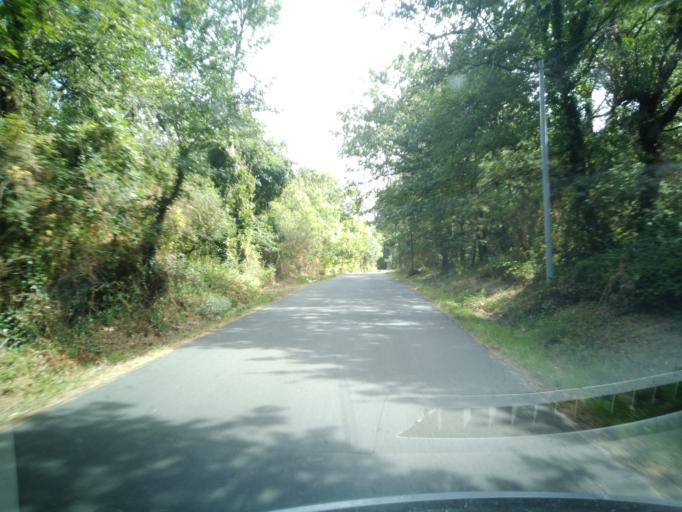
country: FR
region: Poitou-Charentes
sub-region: Departement de la Charente-Maritime
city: Chaillevette
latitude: 45.7164
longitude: -1.0765
